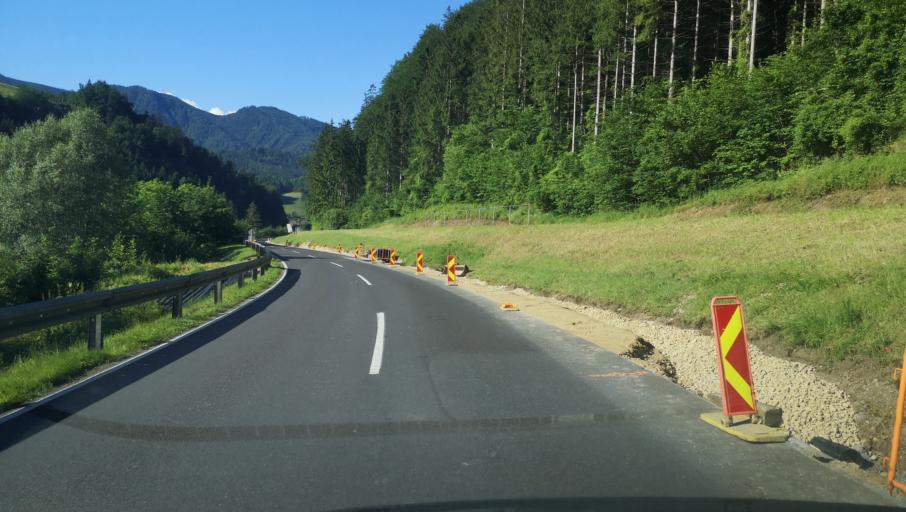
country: AT
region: Lower Austria
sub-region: Politischer Bezirk Amstetten
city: Opponitz
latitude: 47.8878
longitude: 14.8244
